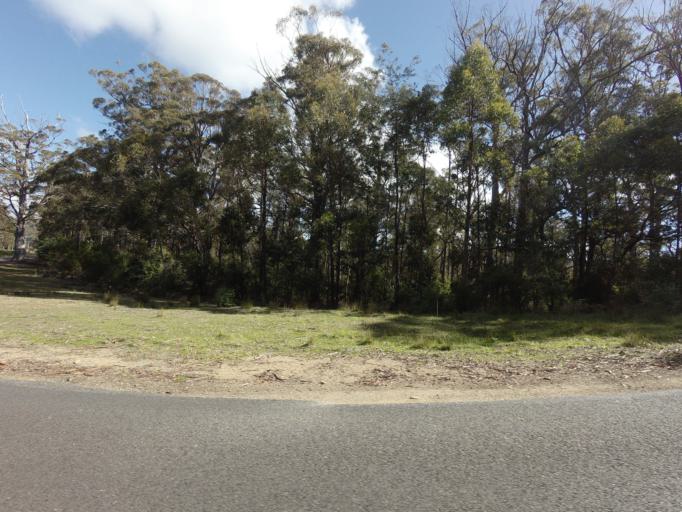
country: AU
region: Tasmania
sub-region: Break O'Day
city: St Helens
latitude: -41.6403
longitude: 148.2428
